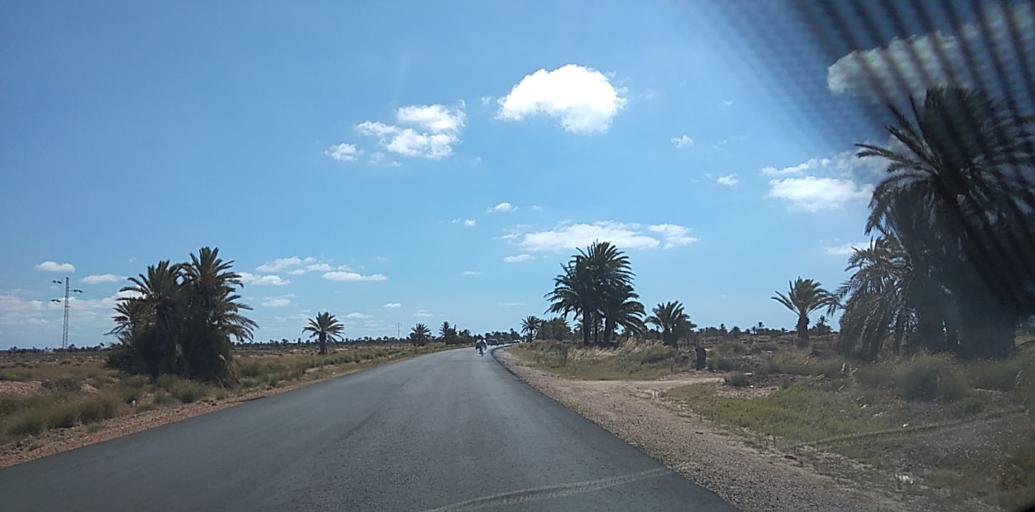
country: TN
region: Safaqis
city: Al Qarmadah
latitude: 34.6587
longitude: 11.1041
